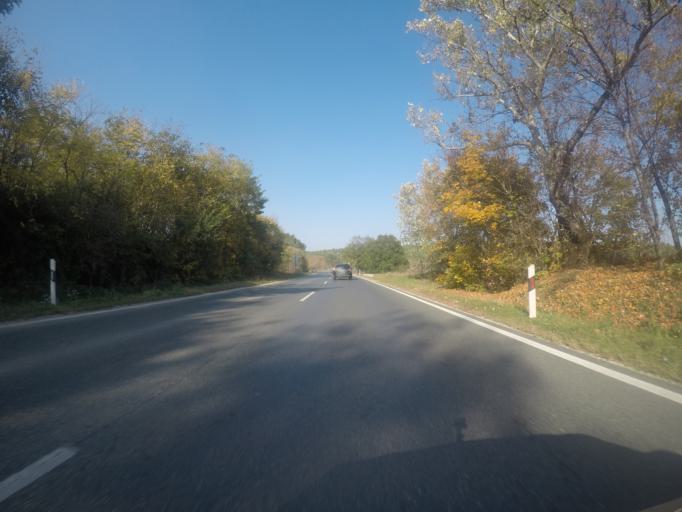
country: HU
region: Tolna
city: Paks
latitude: 46.6864
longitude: 18.8881
